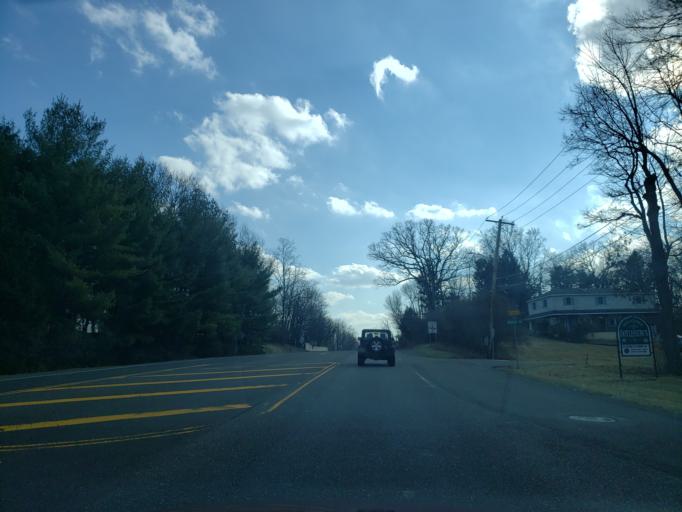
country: US
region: Pennsylvania
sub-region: Bucks County
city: Doylestown
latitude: 40.2977
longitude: -75.1280
